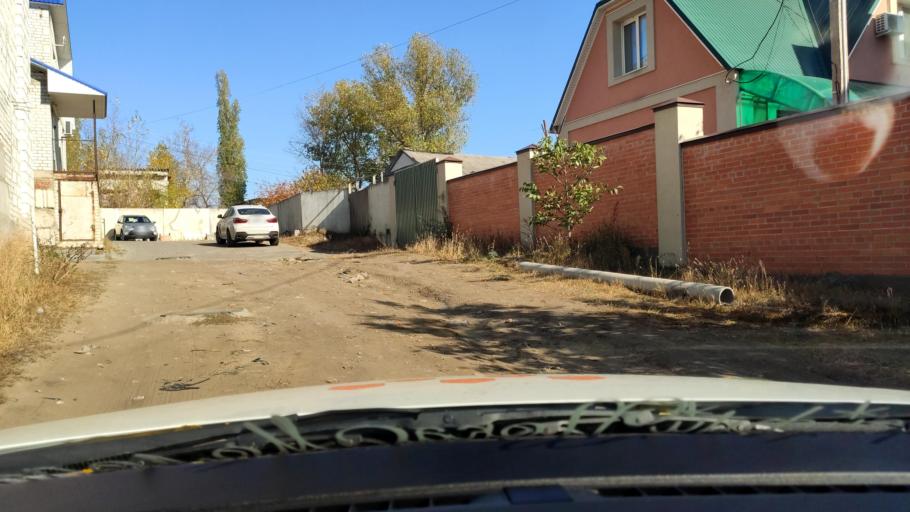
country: RU
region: Voronezj
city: Pridonskoy
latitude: 51.6855
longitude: 39.0650
